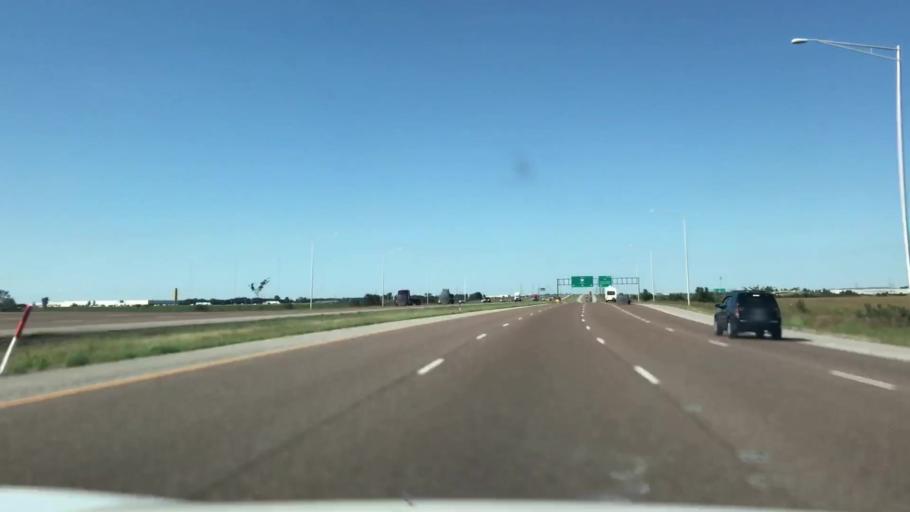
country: US
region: Illinois
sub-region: Madison County
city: Pontoon Beach
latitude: 38.7459
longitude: -90.0434
